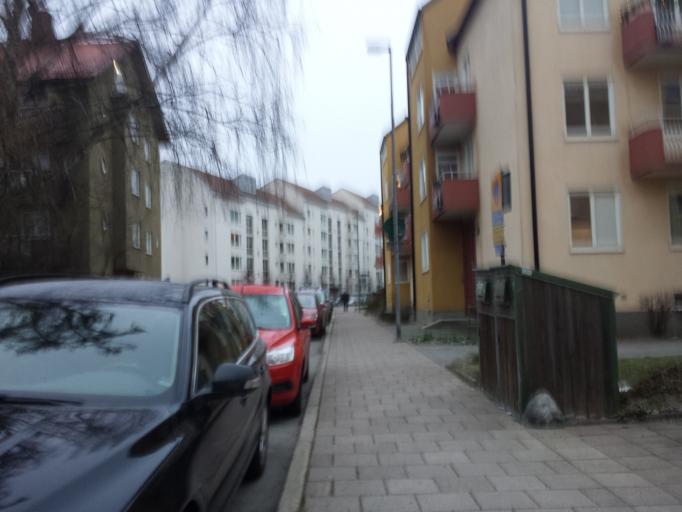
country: SE
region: Stockholm
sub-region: Solna Kommun
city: Solna
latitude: 59.3620
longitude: 18.0185
